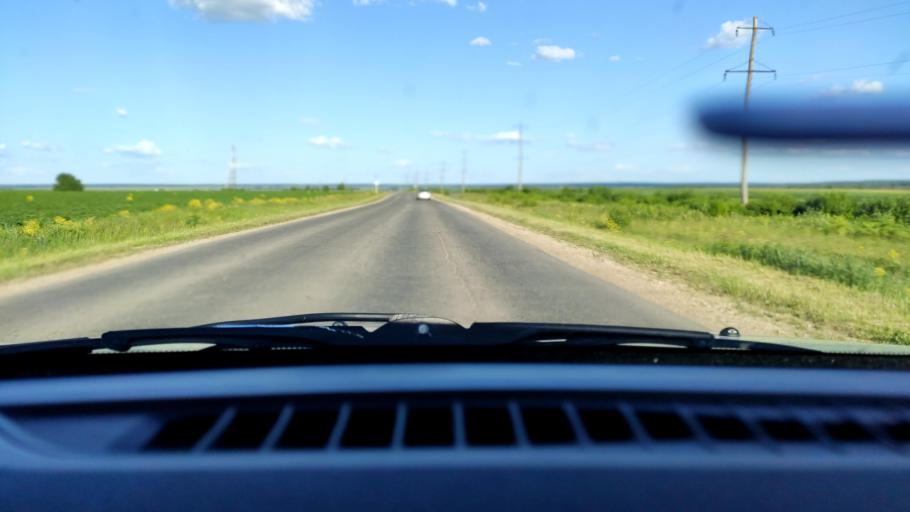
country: RU
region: Perm
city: Orda
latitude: 57.1902
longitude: 56.8662
